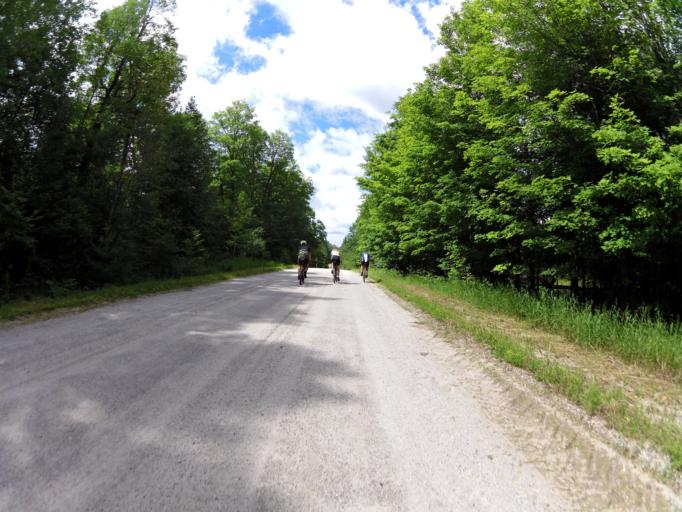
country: CA
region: Ontario
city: Perth
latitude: 45.0462
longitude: -76.4811
